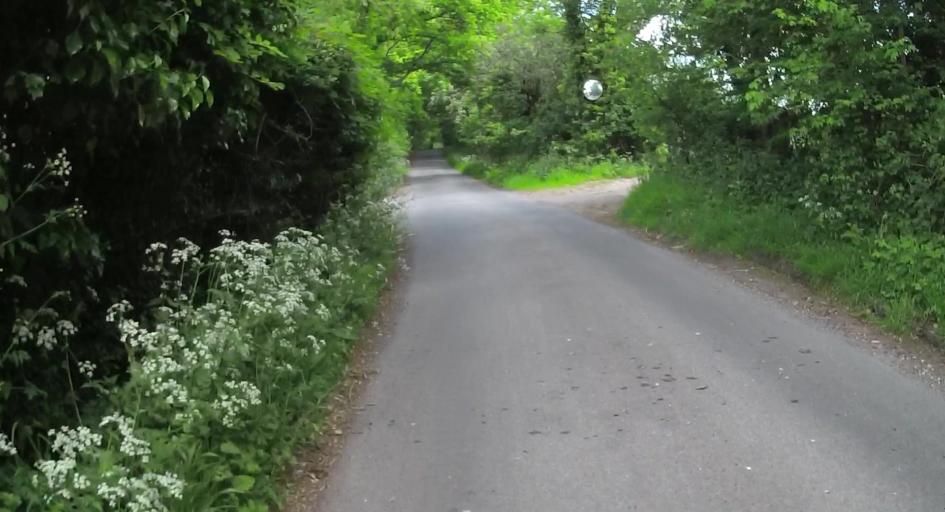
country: GB
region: England
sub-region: Hampshire
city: Fleet
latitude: 51.2357
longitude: -0.8475
